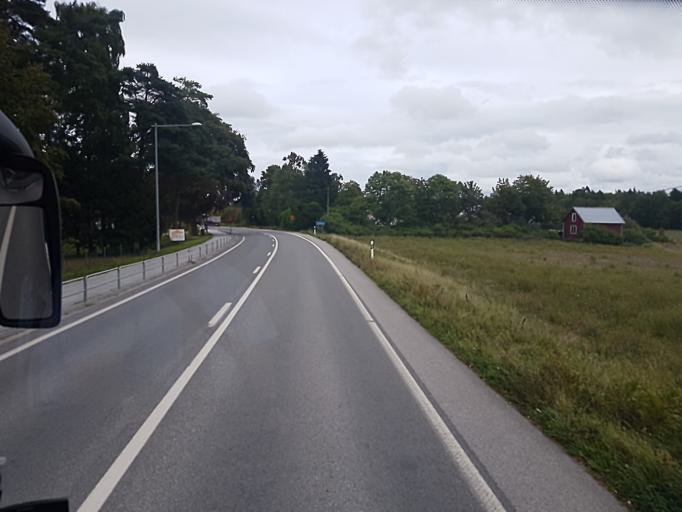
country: SE
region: Gotland
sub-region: Gotland
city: Vibble
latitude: 57.5984
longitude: 18.2500
